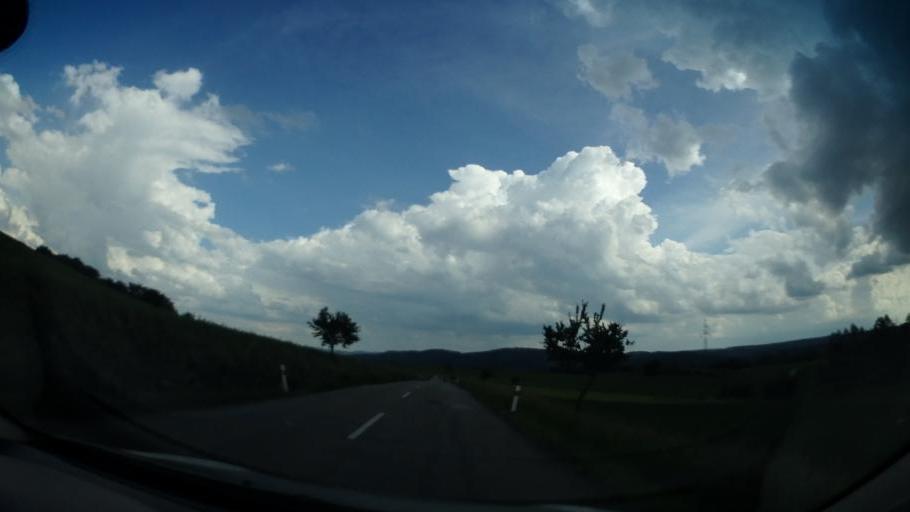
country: CZ
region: South Moravian
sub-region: Okres Brno-Venkov
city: Dolni Loucky
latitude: 49.3838
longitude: 16.3416
